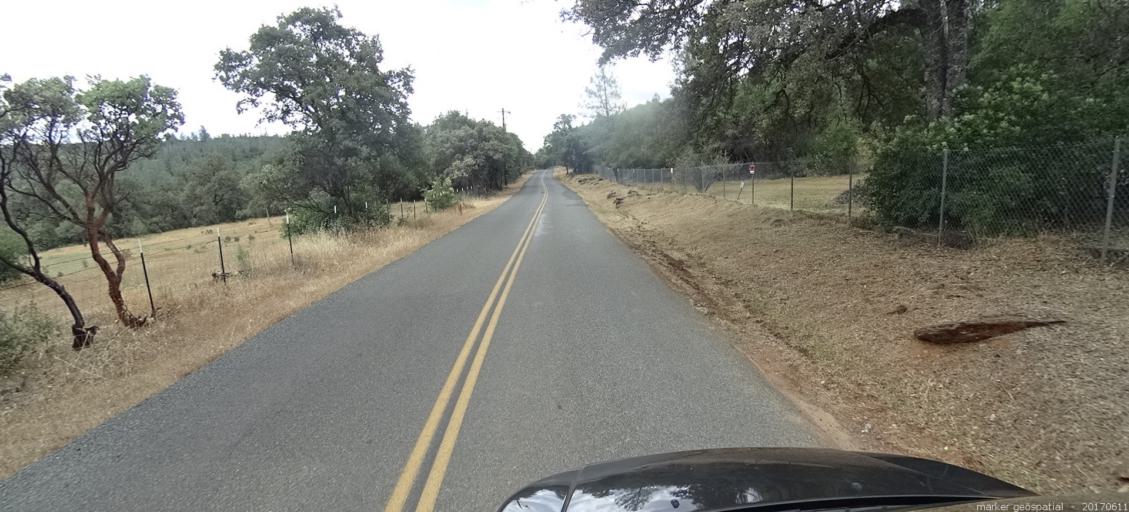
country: US
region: California
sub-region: Butte County
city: Berry Creek
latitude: 39.6379
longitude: -121.5282
